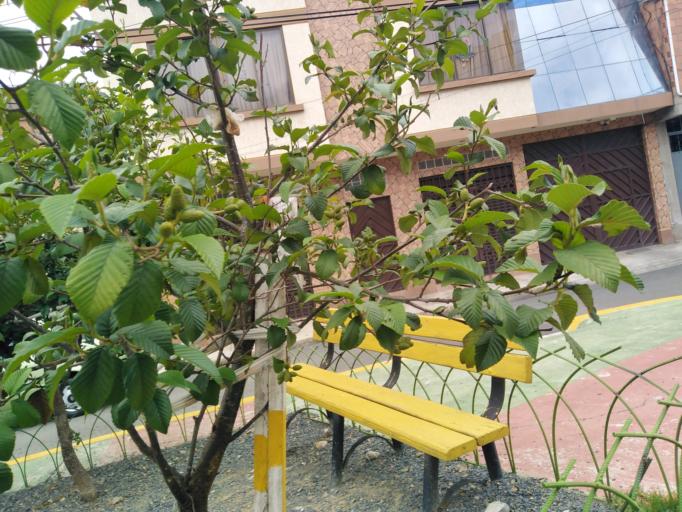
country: BO
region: La Paz
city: La Paz
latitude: -16.5129
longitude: -68.1378
